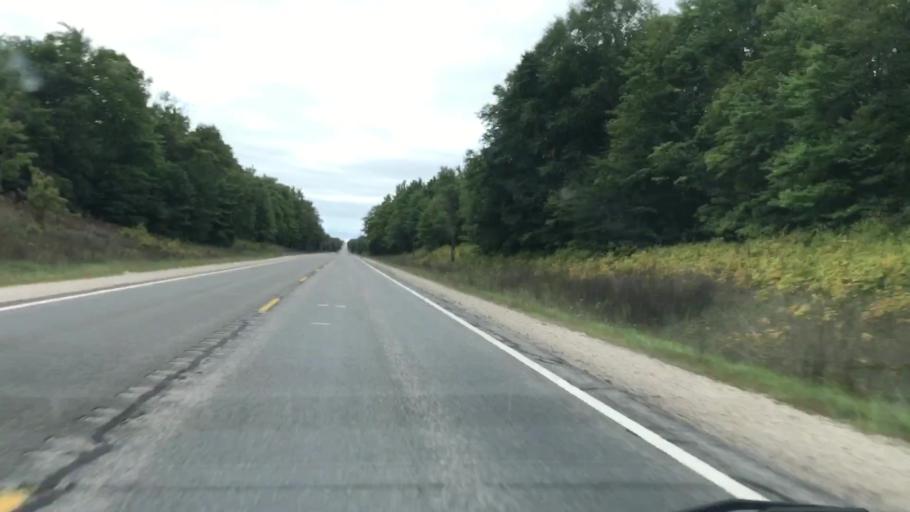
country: US
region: Michigan
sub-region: Luce County
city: Newberry
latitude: 46.2435
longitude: -85.5723
